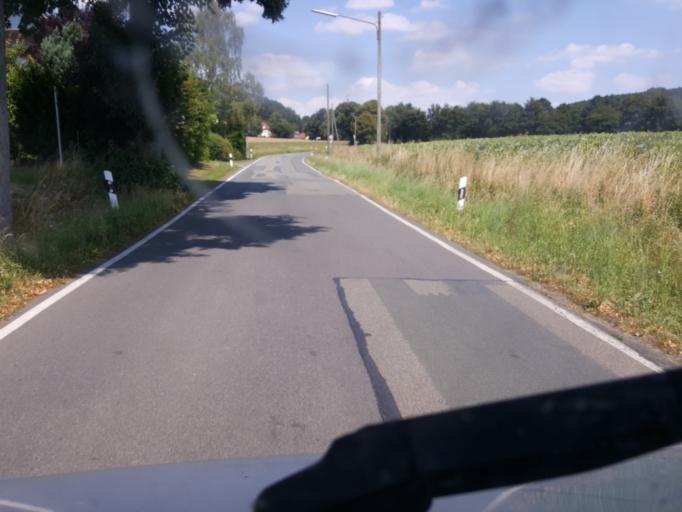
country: DE
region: North Rhine-Westphalia
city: Bad Oeynhausen
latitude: 52.2608
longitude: 8.7633
